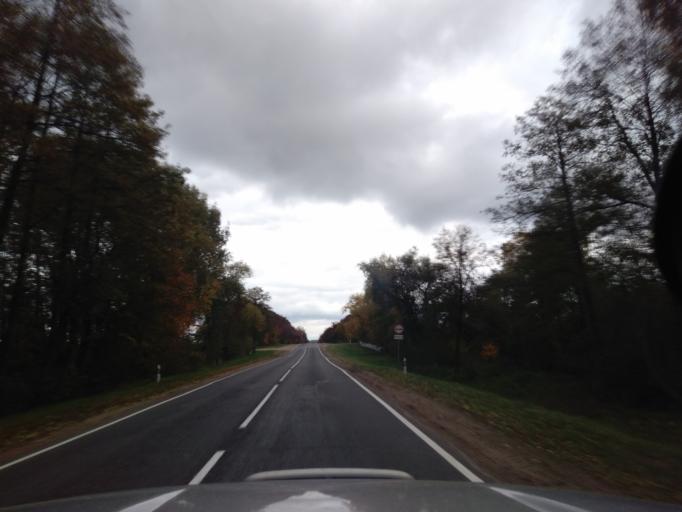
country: BY
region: Minsk
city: Slutsk
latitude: 53.2221
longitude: 27.3730
